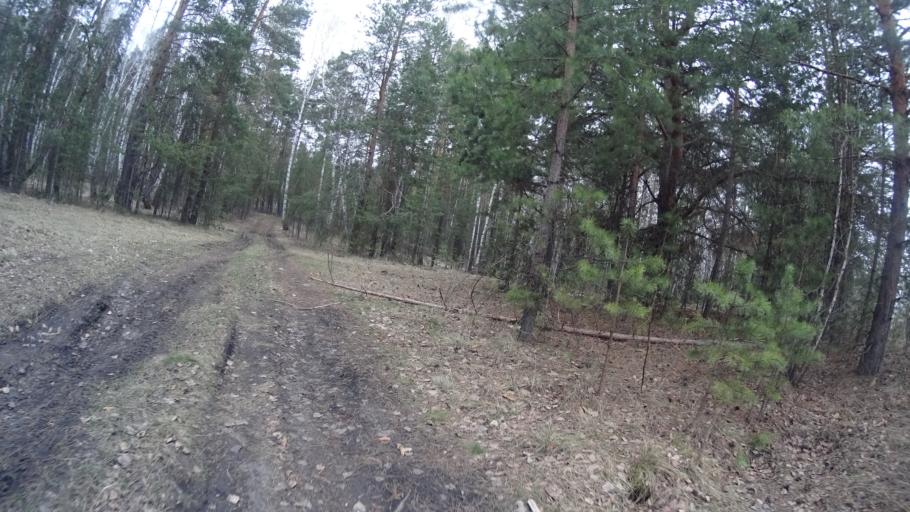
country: RU
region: Chelyabinsk
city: Yuzhnoural'sk
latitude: 54.4950
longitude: 61.2708
